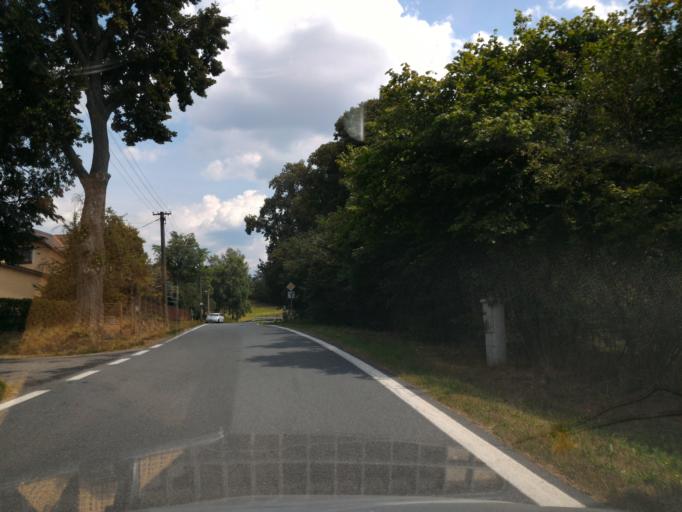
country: CZ
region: Vysocina
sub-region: Okres Havlickuv Brod
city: Havlickuv Brod
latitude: 49.6055
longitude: 15.6519
